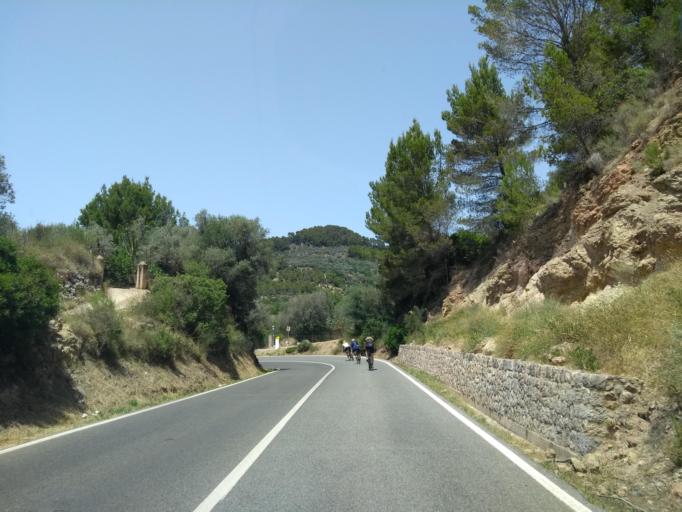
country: ES
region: Balearic Islands
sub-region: Illes Balears
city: Soller
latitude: 39.7833
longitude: 2.7111
